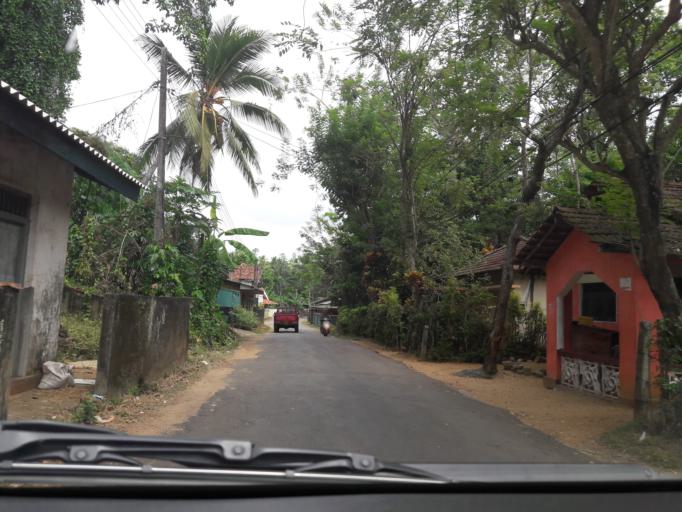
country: LK
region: Southern
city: Hikkaduwa
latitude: 6.1013
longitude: 80.1535
